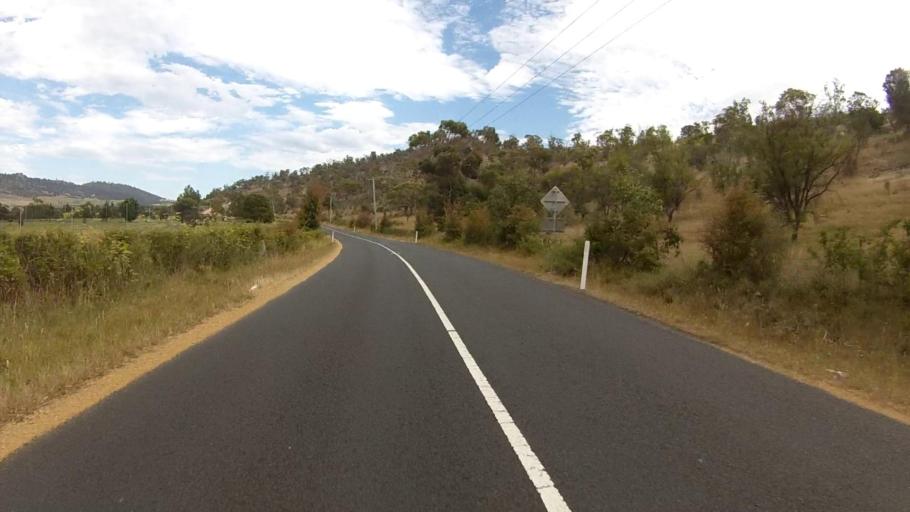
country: AU
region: Tasmania
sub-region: Clarence
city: Cambridge
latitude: -42.7394
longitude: 147.4196
